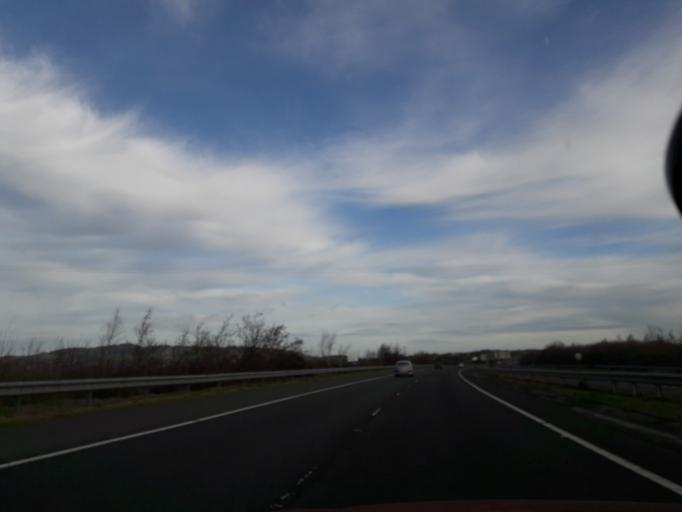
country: GB
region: Northern Ireland
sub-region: Newry and Mourne District
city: Newry
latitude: 54.1142
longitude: -6.3650
